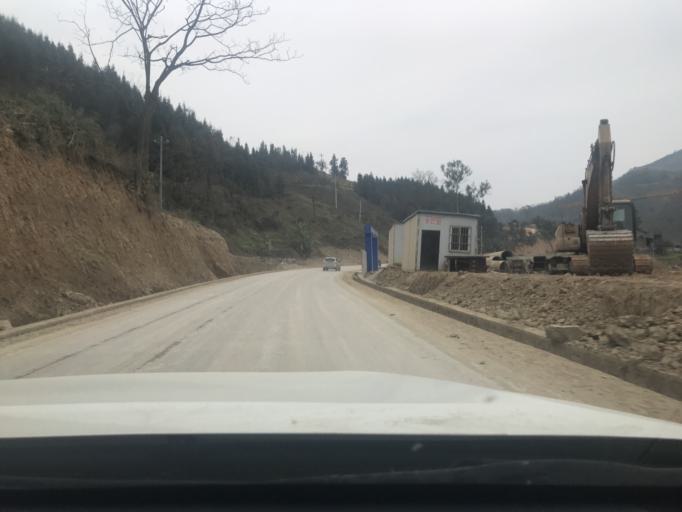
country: CN
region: Guangxi Zhuangzu Zizhiqu
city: Xinzhou
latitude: 25.0090
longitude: 105.8515
